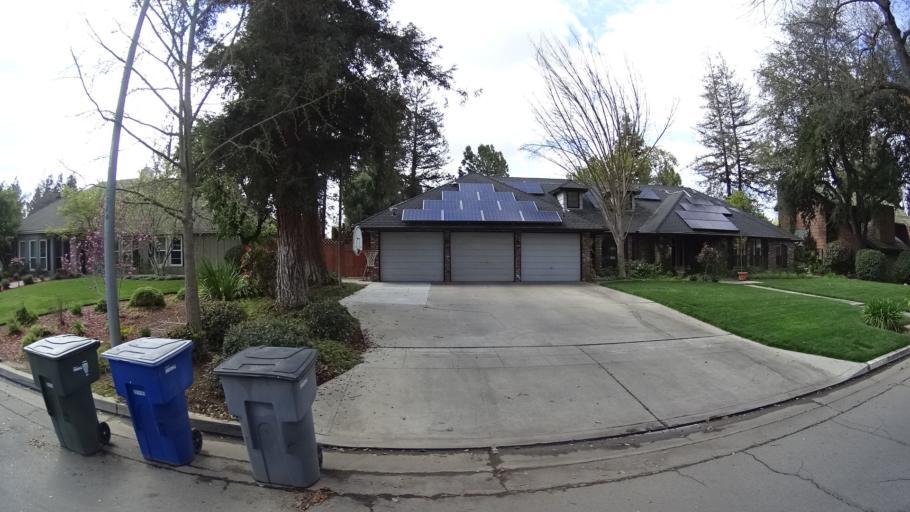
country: US
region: California
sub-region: Fresno County
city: Fresno
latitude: 36.8394
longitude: -119.8627
